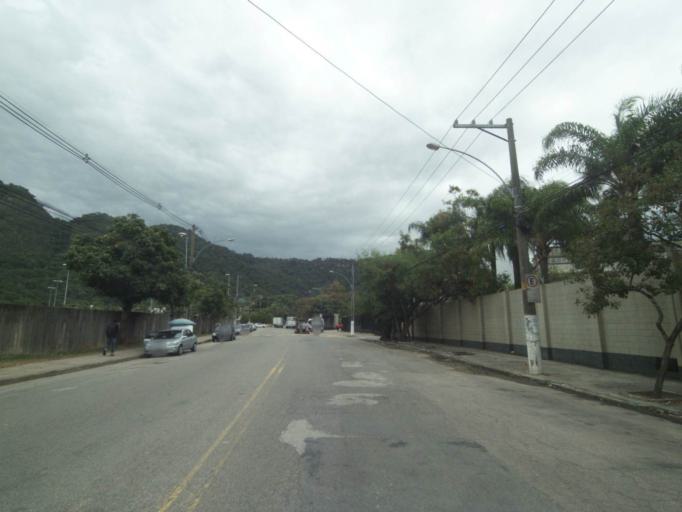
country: BR
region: Rio de Janeiro
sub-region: Nilopolis
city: Nilopolis
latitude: -22.9622
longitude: -43.4042
